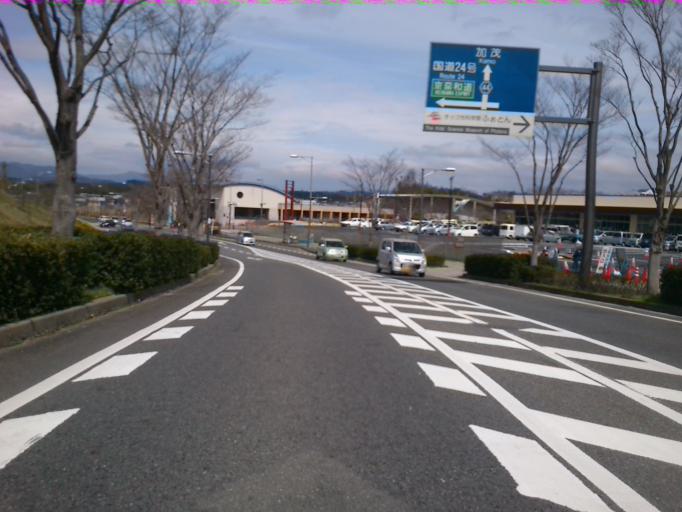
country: JP
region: Nara
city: Nara-shi
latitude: 34.7140
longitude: 135.8338
